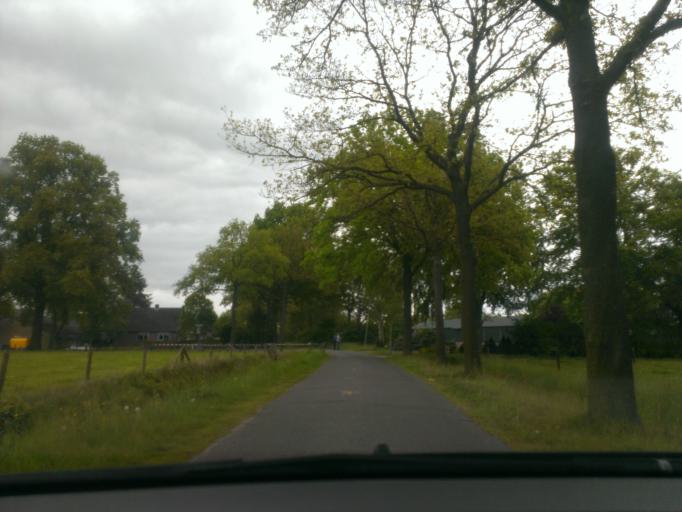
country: NL
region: Gelderland
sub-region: Gemeente Epe
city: Emst
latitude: 52.3359
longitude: 5.9550
